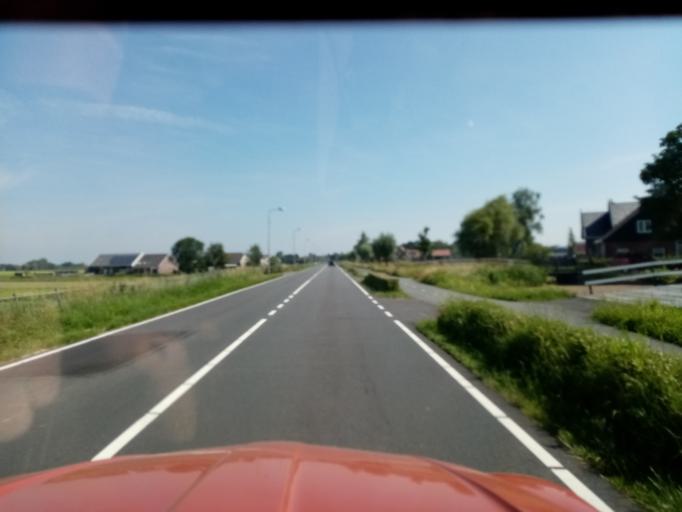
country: NL
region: South Holland
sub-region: Gemeente Kaag en Braassem
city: Leimuiden
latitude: 52.1742
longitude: 4.7040
